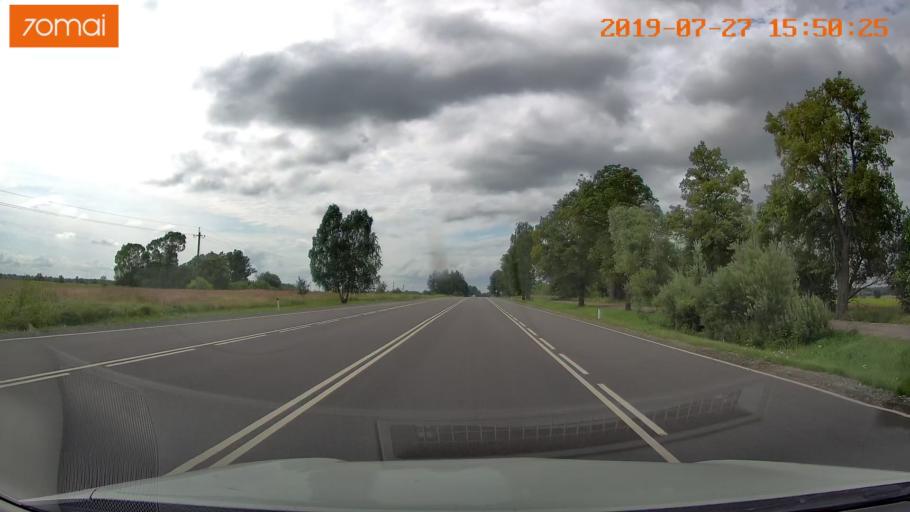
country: RU
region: Kaliningrad
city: Ozersk
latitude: 54.6007
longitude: 22.0075
